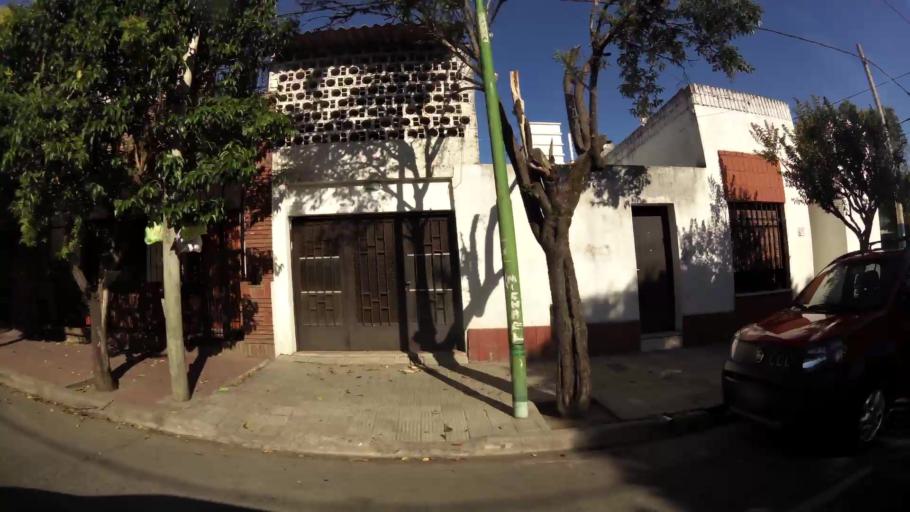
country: AR
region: Cordoba
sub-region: Departamento de Capital
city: Cordoba
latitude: -31.3903
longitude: -64.1708
